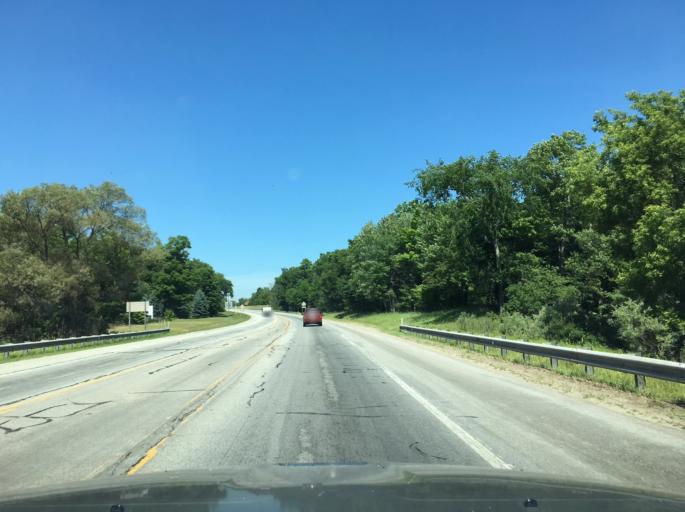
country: US
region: Michigan
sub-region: Osceola County
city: Reed City
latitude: 43.8852
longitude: -85.5130
